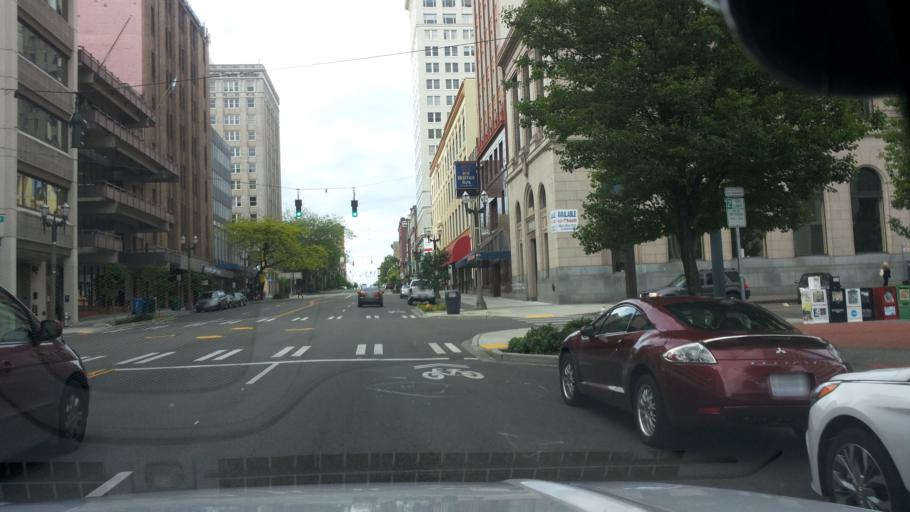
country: US
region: Washington
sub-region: Pierce County
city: Tacoma
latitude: 47.2521
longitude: -122.4383
